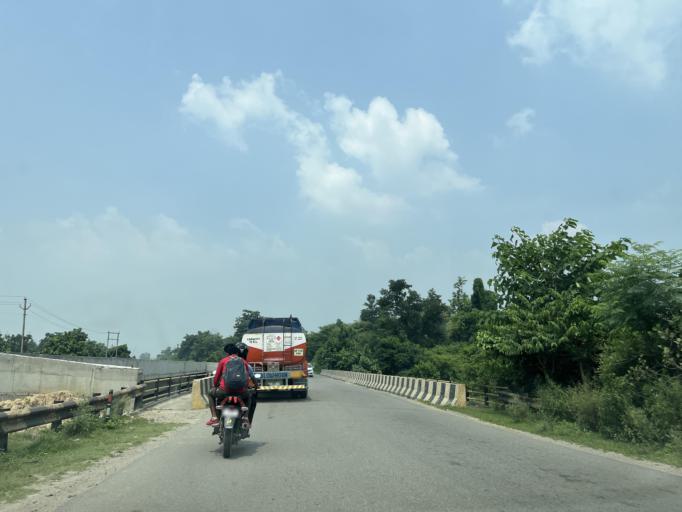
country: IN
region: Uttarakhand
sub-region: Haridwar
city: Haridwar
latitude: 29.8556
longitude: 78.1866
